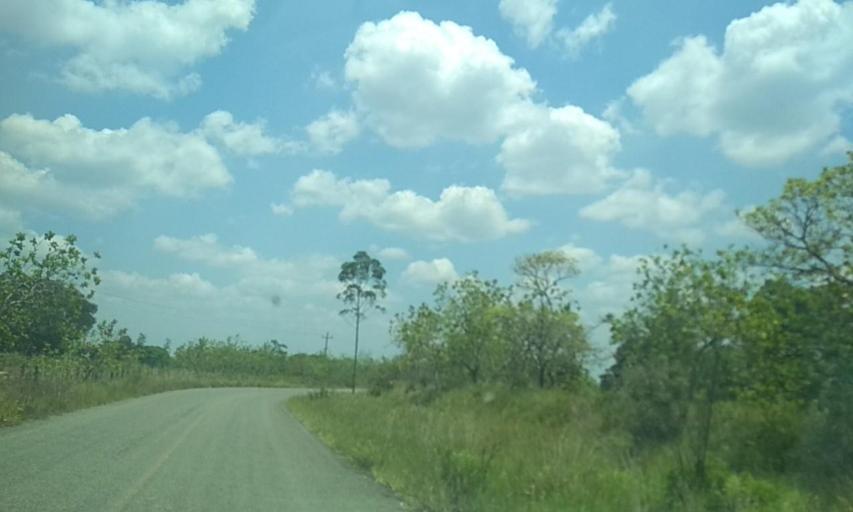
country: MX
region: Tabasco
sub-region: Huimanguillo
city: Francisco Rueda
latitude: 17.7857
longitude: -93.8302
